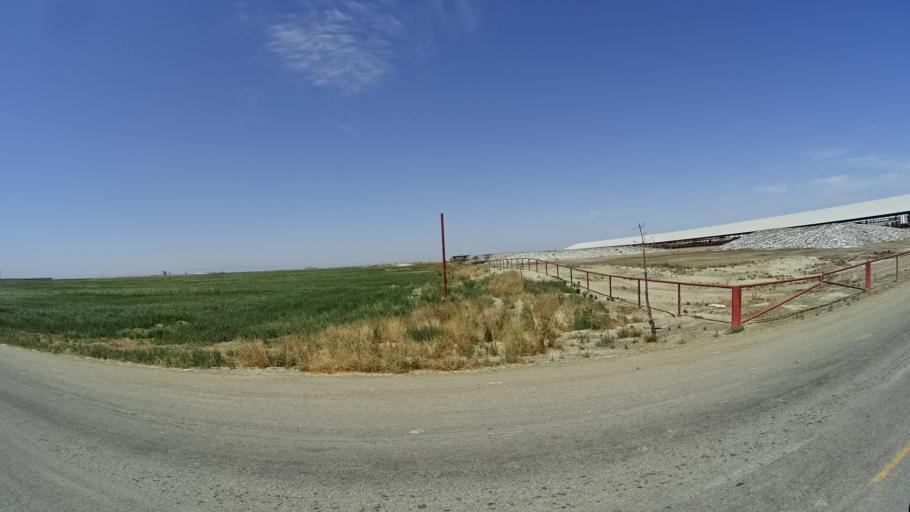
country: US
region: California
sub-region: Kings County
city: Armona
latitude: 36.2038
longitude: -119.6907
